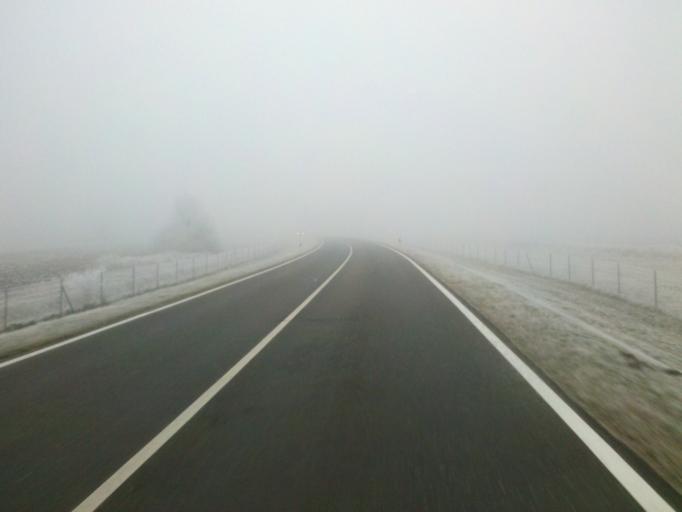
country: HR
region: Varazdinska
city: Jalkovec
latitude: 46.2695
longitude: 16.3391
